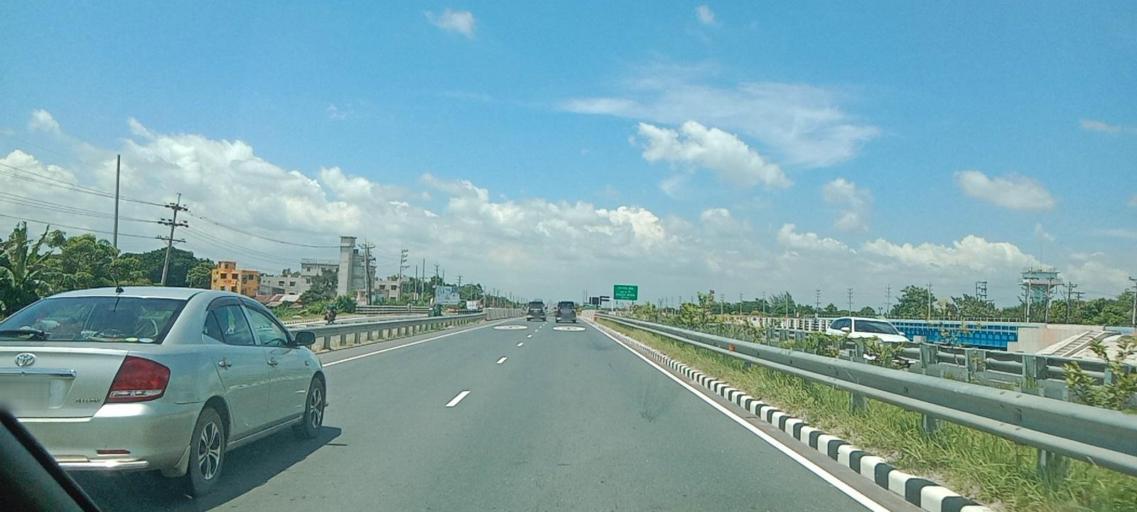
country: BD
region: Dhaka
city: Dohar
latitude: 23.4968
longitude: 90.2710
